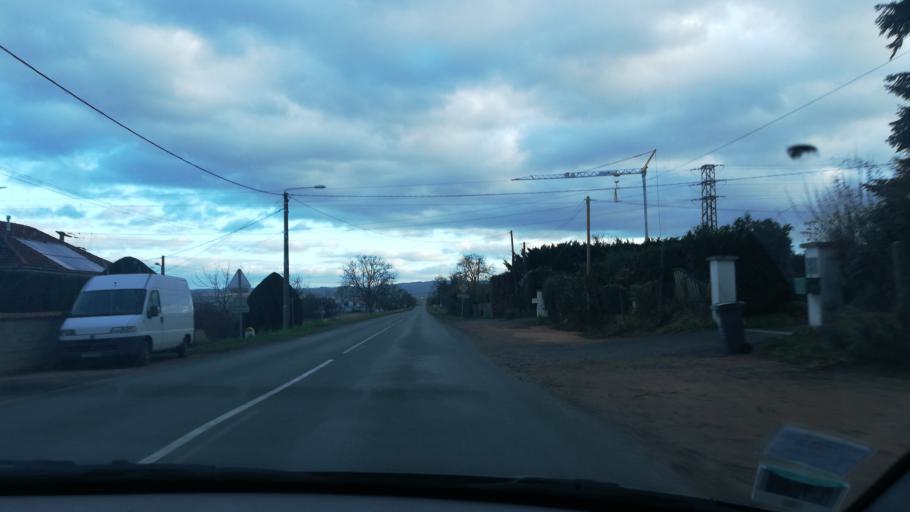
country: FR
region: Auvergne
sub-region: Departement du Puy-de-Dome
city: Vertaizon
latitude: 45.7704
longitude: 3.2979
